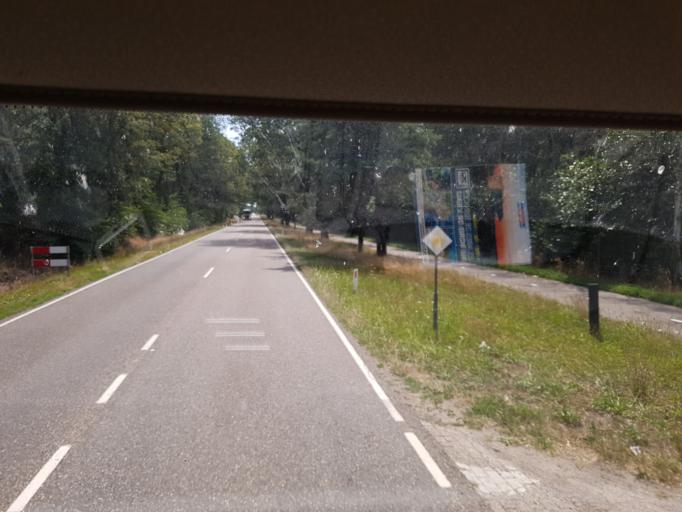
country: NL
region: Limburg
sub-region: Gemeente Leudal
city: Kelpen-Oler
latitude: 51.2585
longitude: 5.7950
